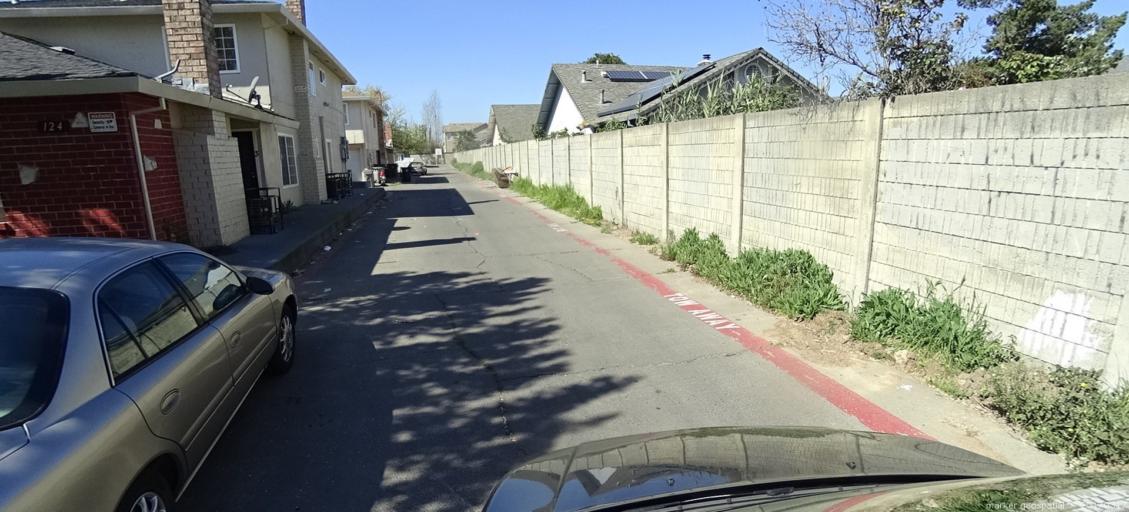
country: US
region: California
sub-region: Sacramento County
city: Parkway
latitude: 38.4834
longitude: -121.4814
